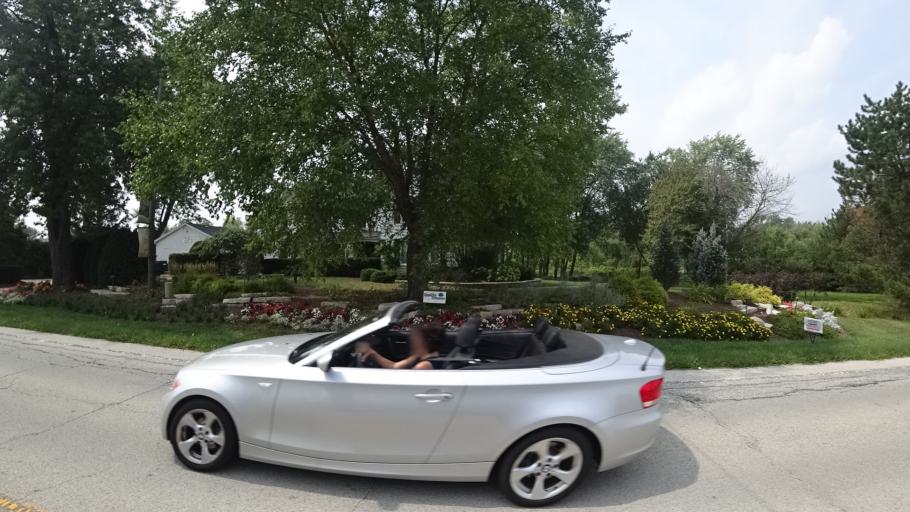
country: US
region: Illinois
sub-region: Will County
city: Goodings Grove
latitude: 41.6167
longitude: -87.9111
